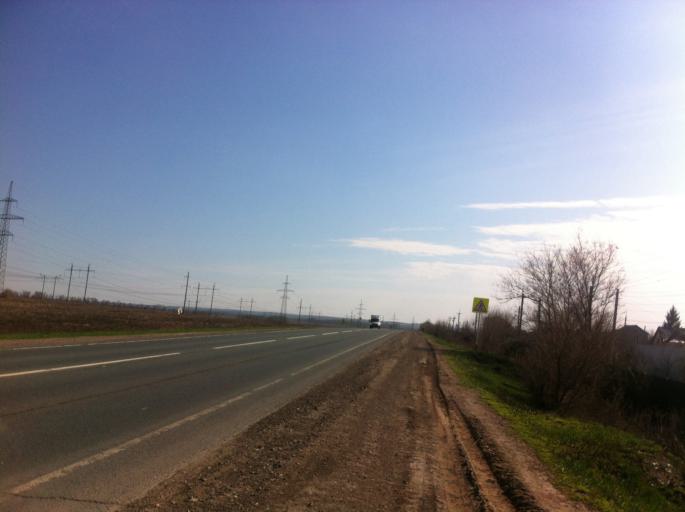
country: RU
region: Samara
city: Smyshlyayevka
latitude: 53.1176
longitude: 50.4154
